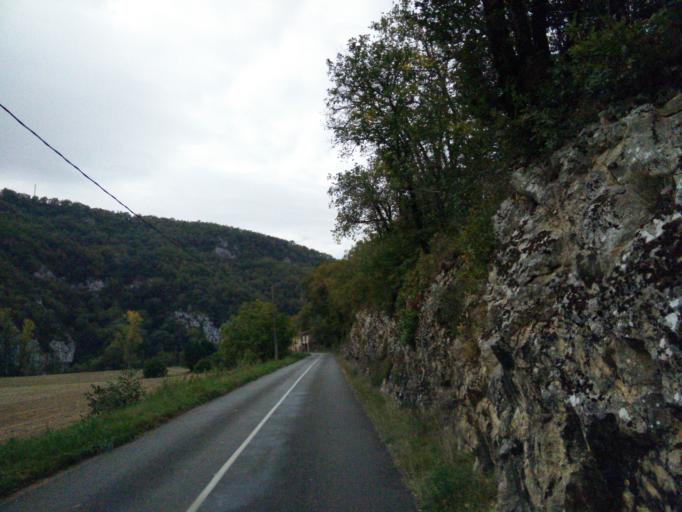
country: FR
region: Midi-Pyrenees
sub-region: Departement du Lot
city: Lalbenque
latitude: 44.4663
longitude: 1.6012
